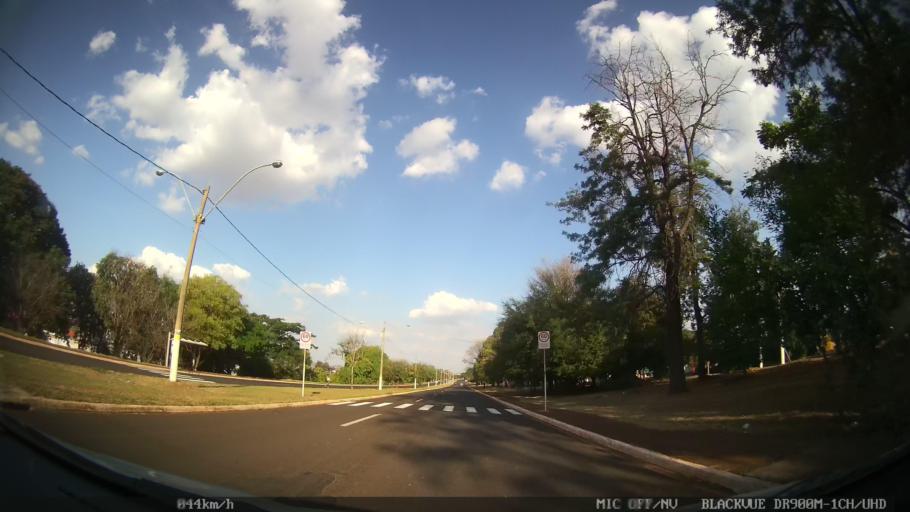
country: BR
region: Sao Paulo
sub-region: Ribeirao Preto
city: Ribeirao Preto
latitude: -21.1328
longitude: -47.8397
